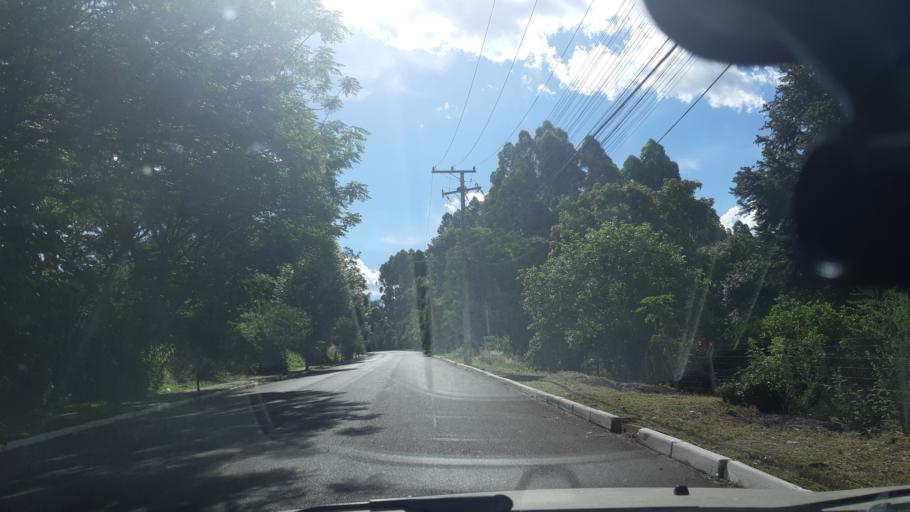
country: BR
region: Rio Grande do Sul
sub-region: Ivoti
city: Ivoti
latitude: -29.6194
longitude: -51.1180
